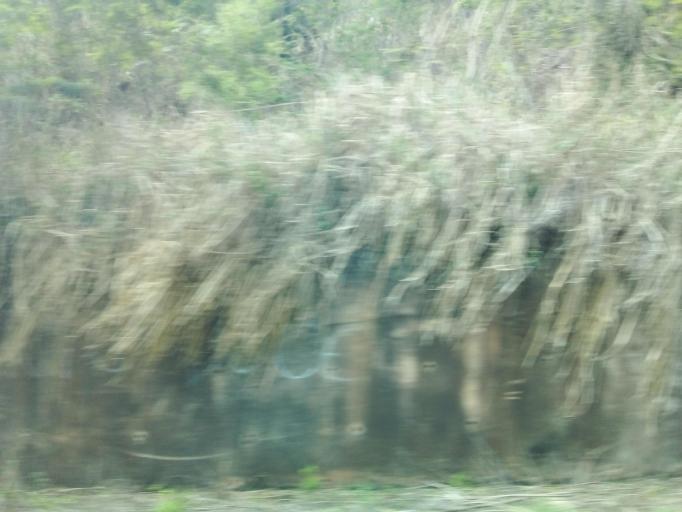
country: BR
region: Minas Gerais
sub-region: Governador Valadares
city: Governador Valadares
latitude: -18.9254
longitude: -42.0196
